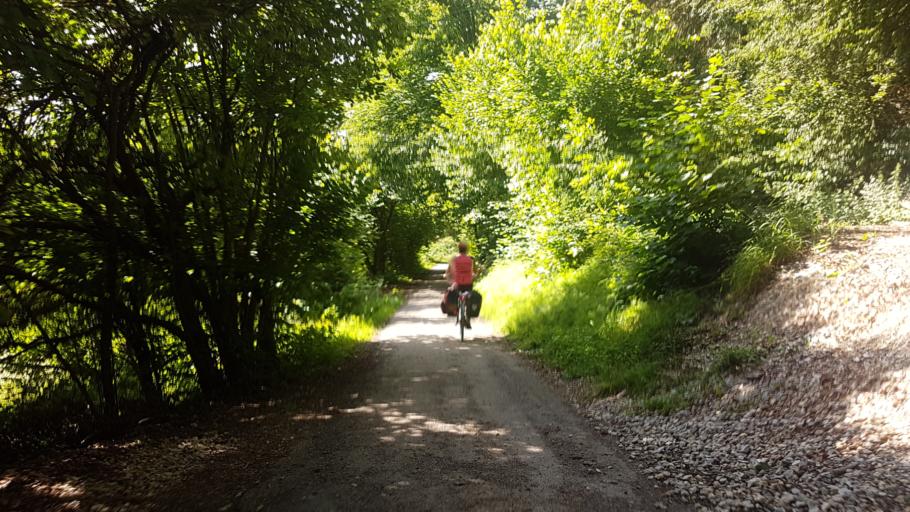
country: DE
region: Bavaria
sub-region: Upper Bavaria
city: Walting
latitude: 48.9437
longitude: 11.3518
